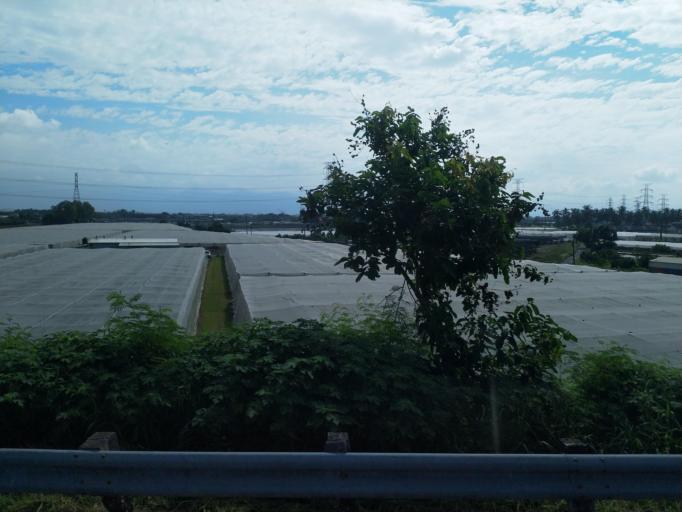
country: TW
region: Taiwan
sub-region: Pingtung
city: Pingtung
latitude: 22.8272
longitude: 120.4890
